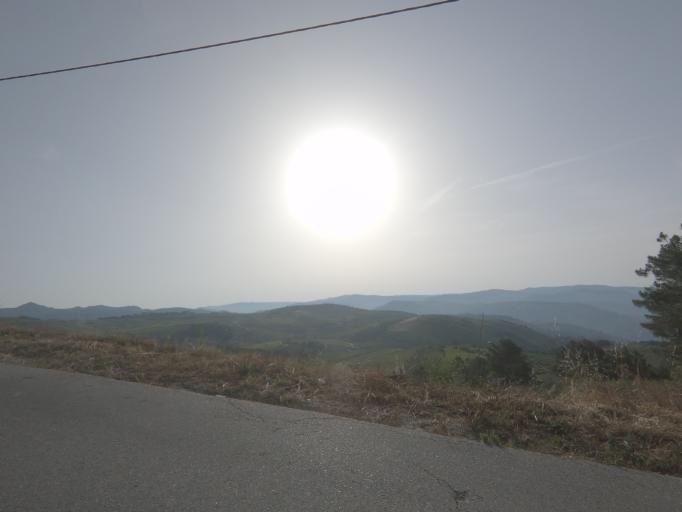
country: PT
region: Viseu
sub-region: Sao Joao da Pesqueira
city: Sao Joao da Pesqueira
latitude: 41.2332
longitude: -7.4666
